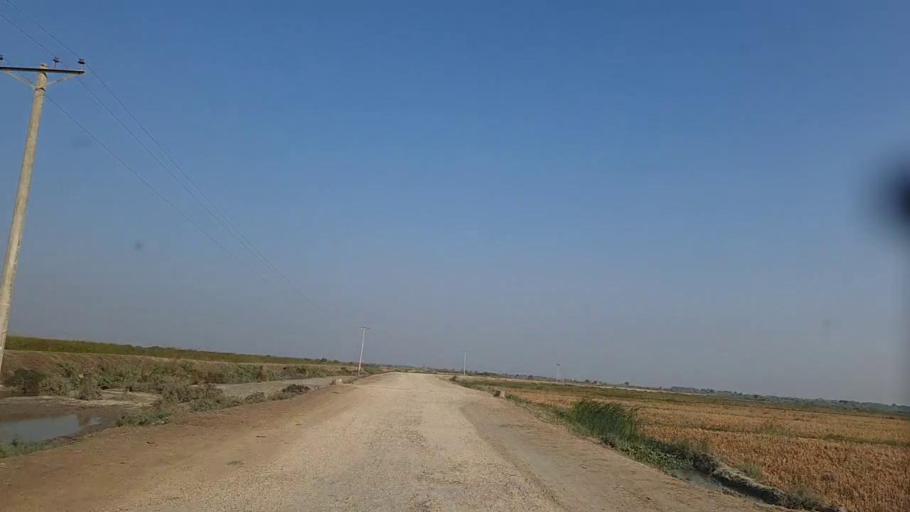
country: PK
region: Sindh
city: Jati
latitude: 24.4615
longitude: 68.2806
